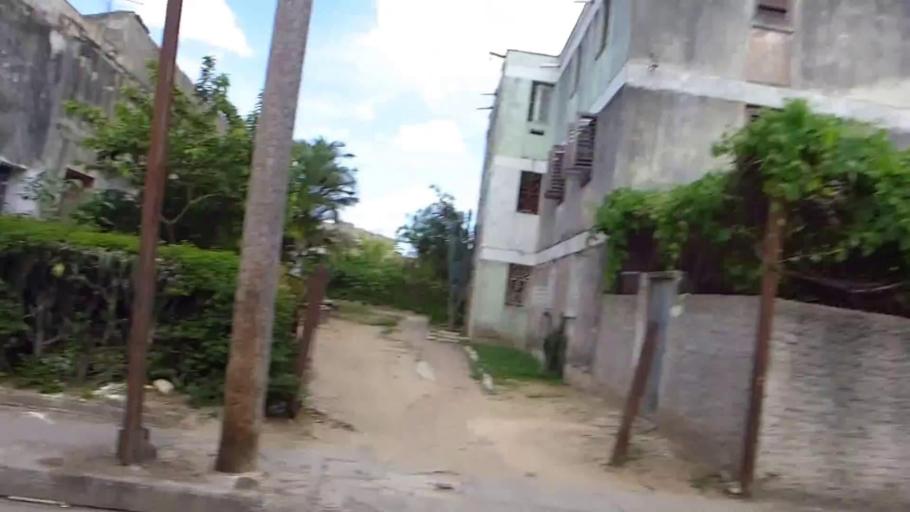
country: CU
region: Camaguey
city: Camaguey
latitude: 21.3856
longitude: -77.9189
